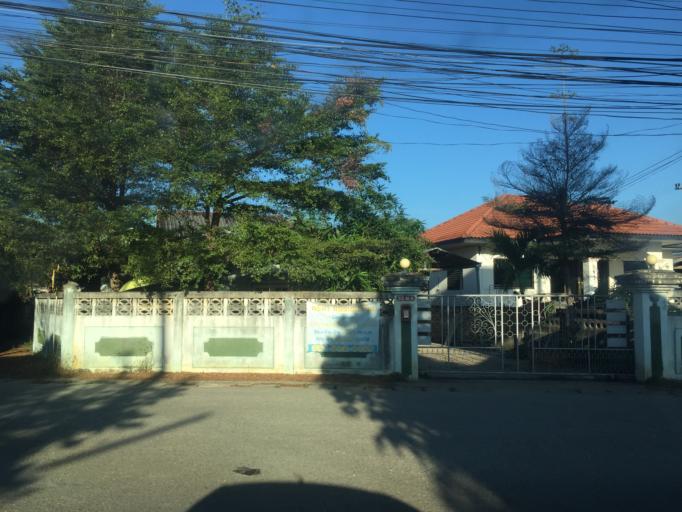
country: TH
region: Lamphun
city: Lamphun
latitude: 18.6084
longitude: 99.0571
